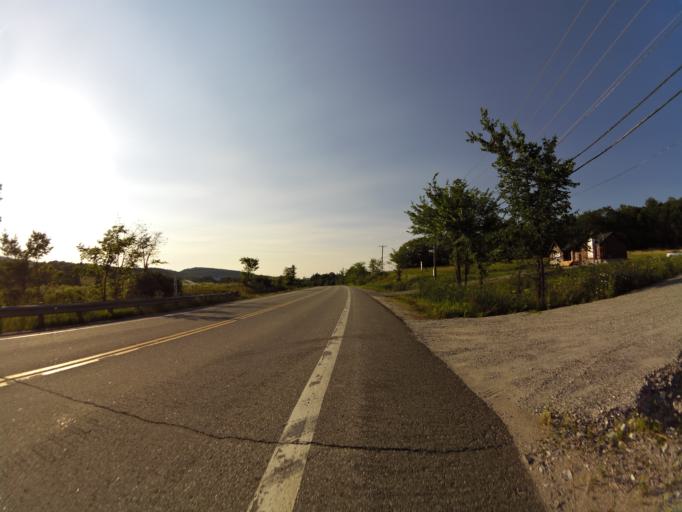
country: CA
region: Quebec
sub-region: Outaouais
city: Wakefield
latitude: 45.5932
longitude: -75.8924
